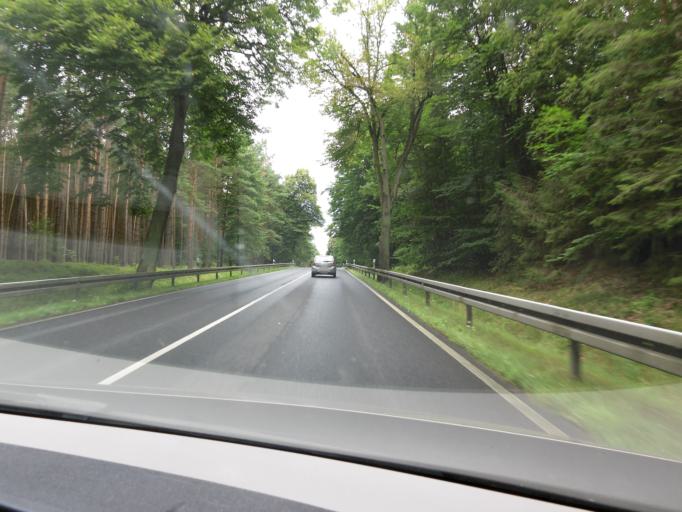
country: DE
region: Brandenburg
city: Furstenberg
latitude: 53.2638
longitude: 13.1164
